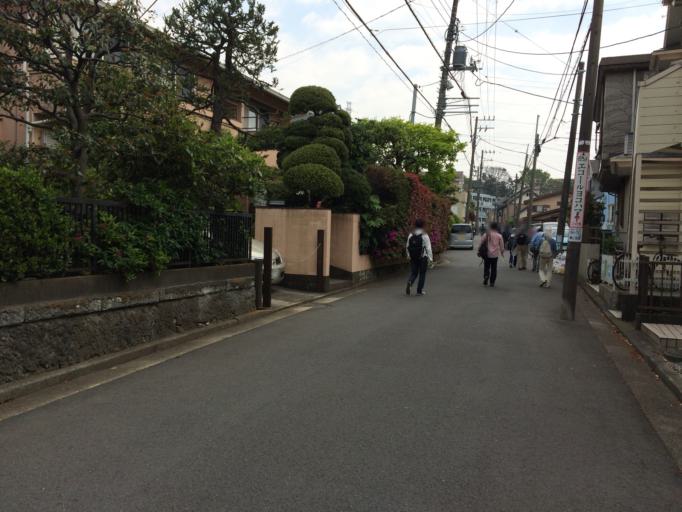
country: JP
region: Kanagawa
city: Yokohama
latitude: 35.5083
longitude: 139.6360
